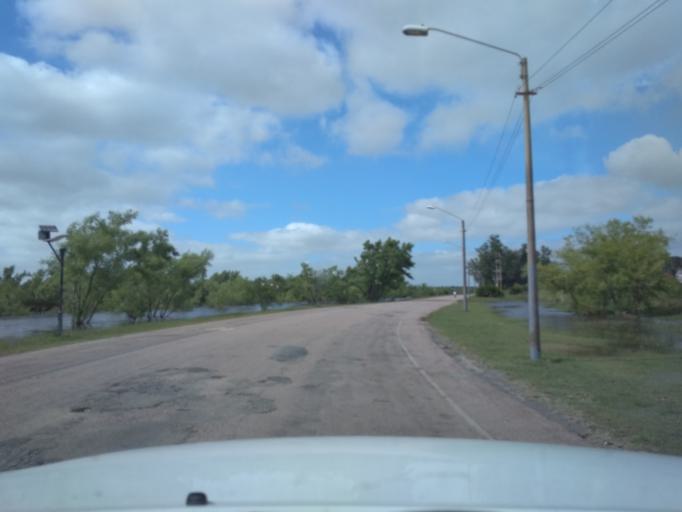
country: UY
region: Florida
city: Florida
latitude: -34.1040
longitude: -56.2038
